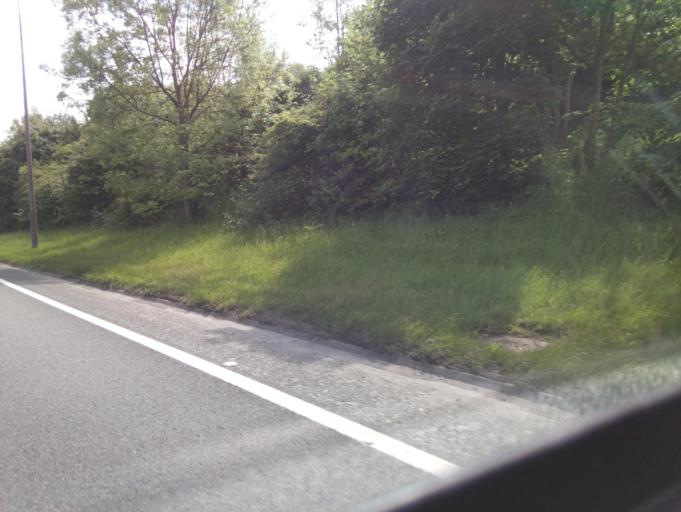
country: GB
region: England
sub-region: Hartlepool
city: Elwick
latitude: 54.7112
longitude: -1.3204
